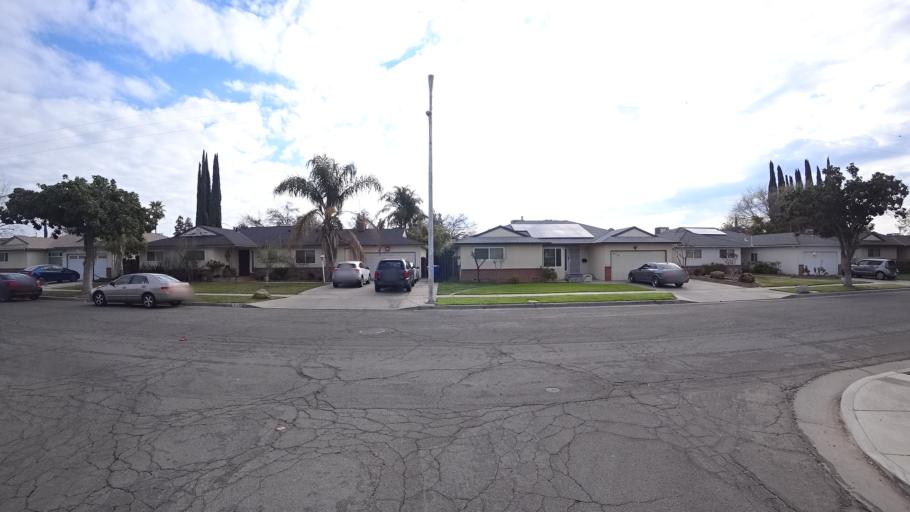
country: US
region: California
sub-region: Fresno County
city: Clovis
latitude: 36.8253
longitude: -119.7642
